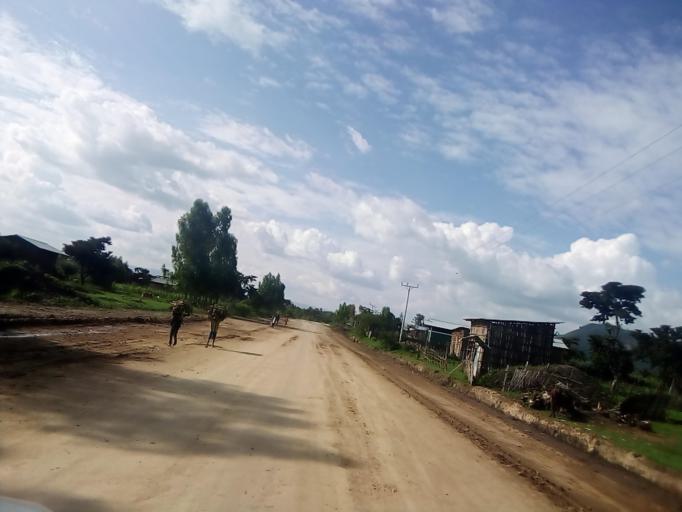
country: ET
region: Southern Nations, Nationalities, and People's Region
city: K'olito
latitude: 7.6097
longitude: 38.0660
